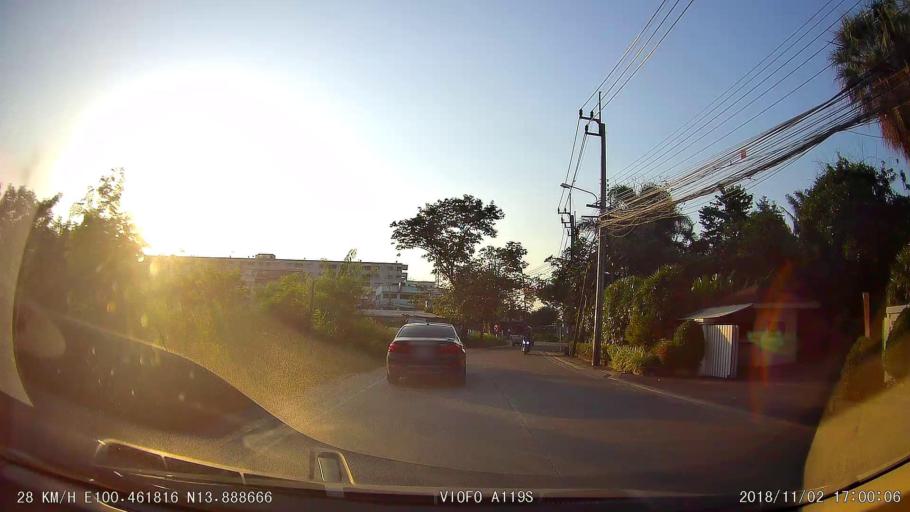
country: TH
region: Nonthaburi
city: Bang Bua Thong
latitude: 13.8887
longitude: 100.4617
